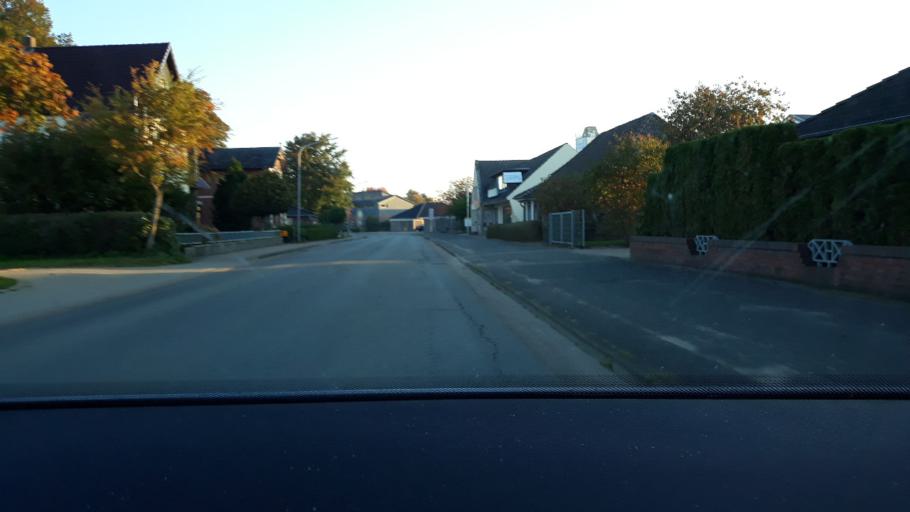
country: DE
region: Schleswig-Holstein
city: Satrup
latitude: 54.6878
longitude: 9.6025
